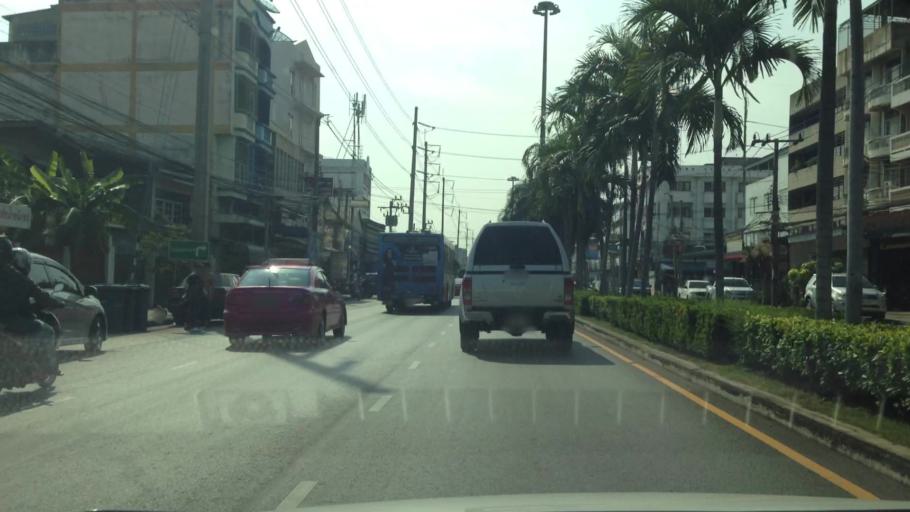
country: TH
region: Samut Prakan
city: Samut Prakan
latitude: 13.5847
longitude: 100.6000
